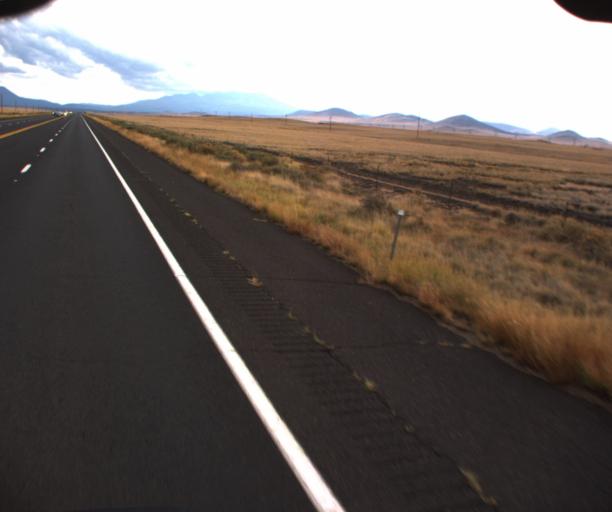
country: US
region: Arizona
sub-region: Coconino County
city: Flagstaff
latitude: 35.6323
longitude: -111.5198
